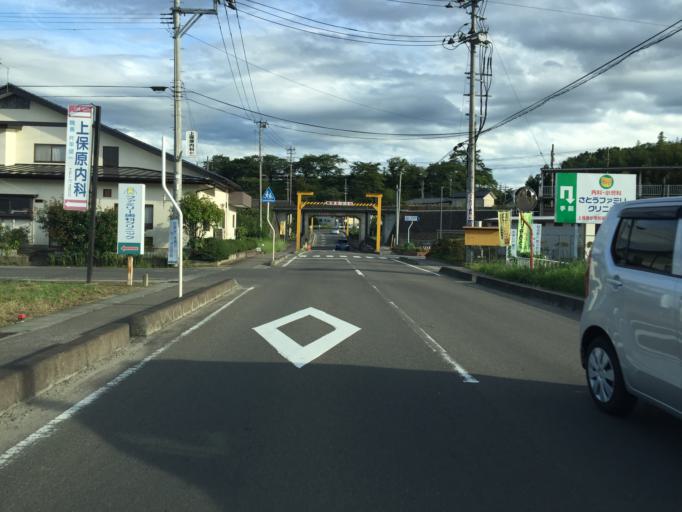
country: JP
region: Fukushima
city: Hobaramachi
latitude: 37.8105
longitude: 140.5435
